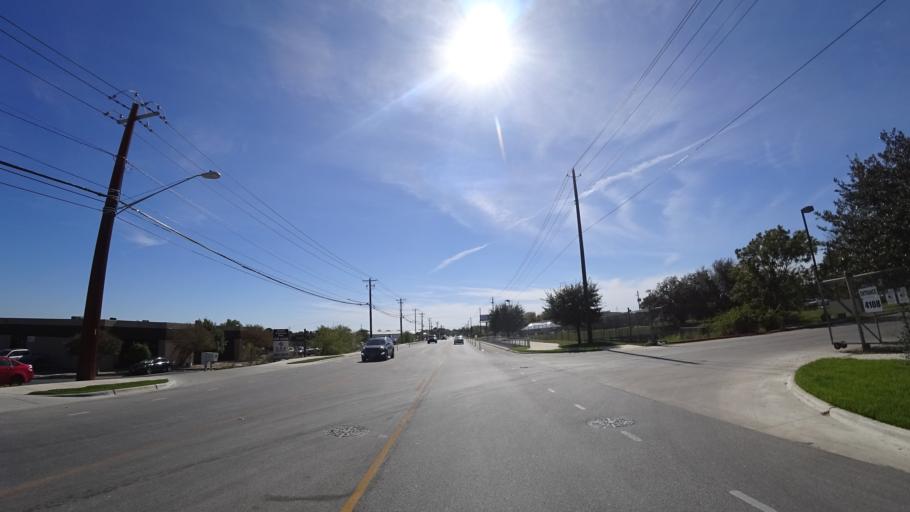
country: US
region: Texas
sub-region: Travis County
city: Austin
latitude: 30.2112
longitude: -97.7377
